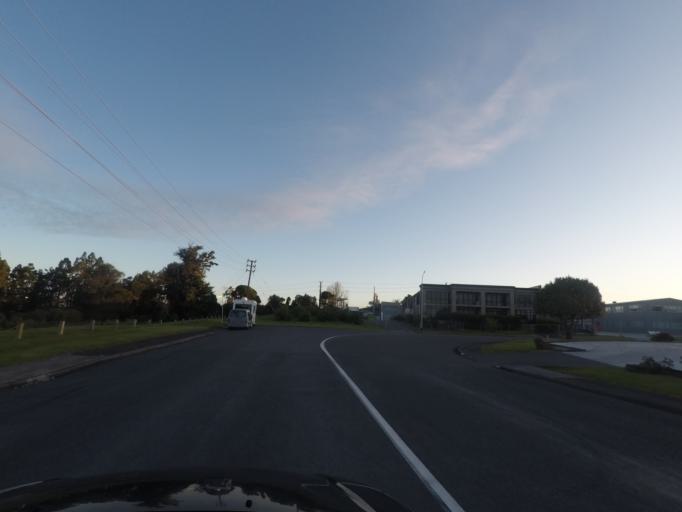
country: NZ
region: Auckland
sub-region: Auckland
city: Rosebank
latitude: -36.8915
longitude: 174.6612
